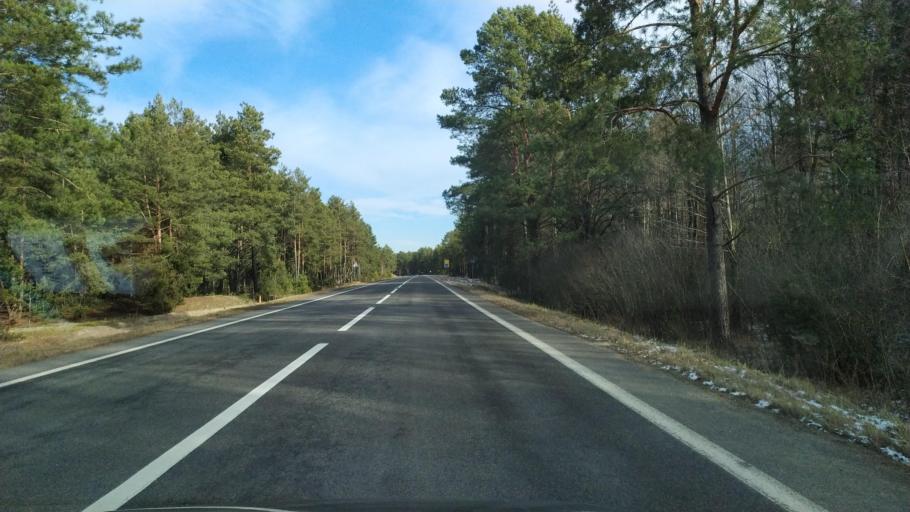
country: BY
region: Brest
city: Zhabinka
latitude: 52.4664
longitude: 24.1483
